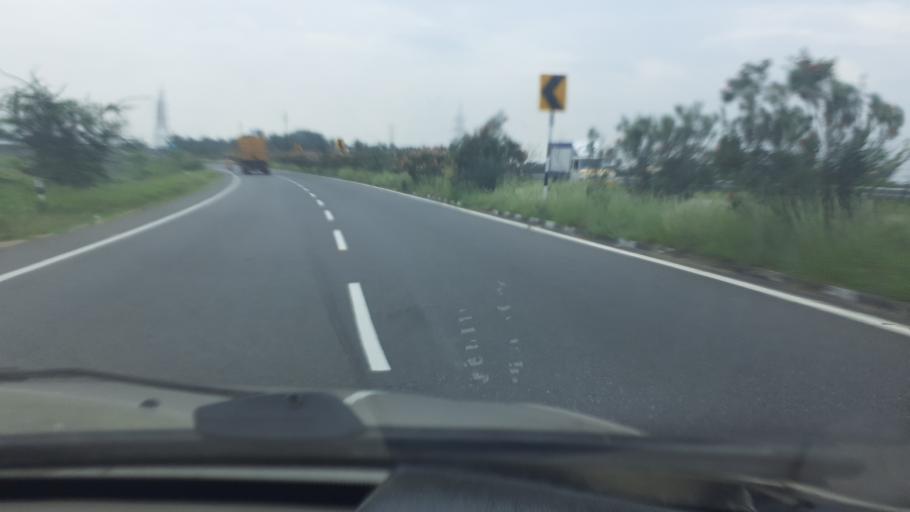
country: IN
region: Tamil Nadu
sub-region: Madurai
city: Tirupparangunram
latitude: 9.8324
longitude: 77.9761
